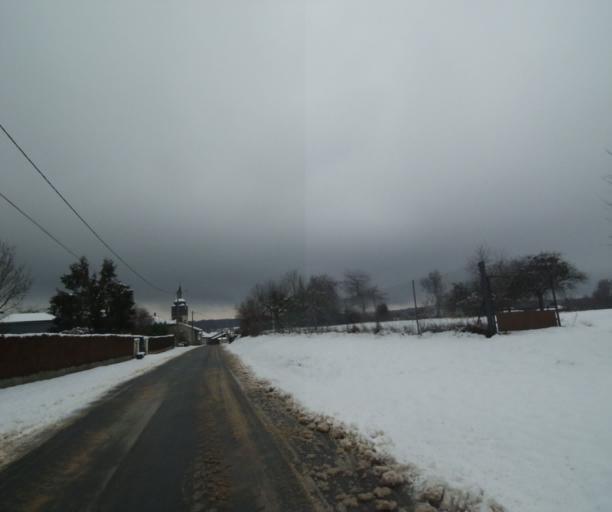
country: FR
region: Champagne-Ardenne
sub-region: Departement de la Haute-Marne
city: Laneuville-a-Remy
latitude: 48.4607
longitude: 4.9183
